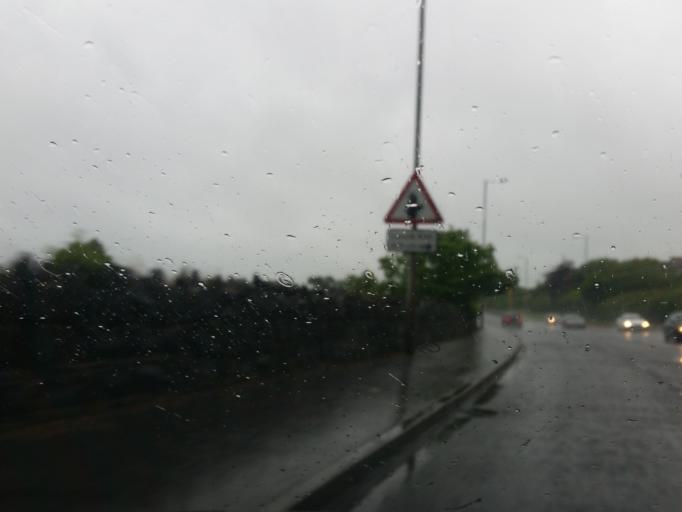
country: GB
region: Northern Ireland
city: Holywood
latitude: 54.6565
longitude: -5.7834
